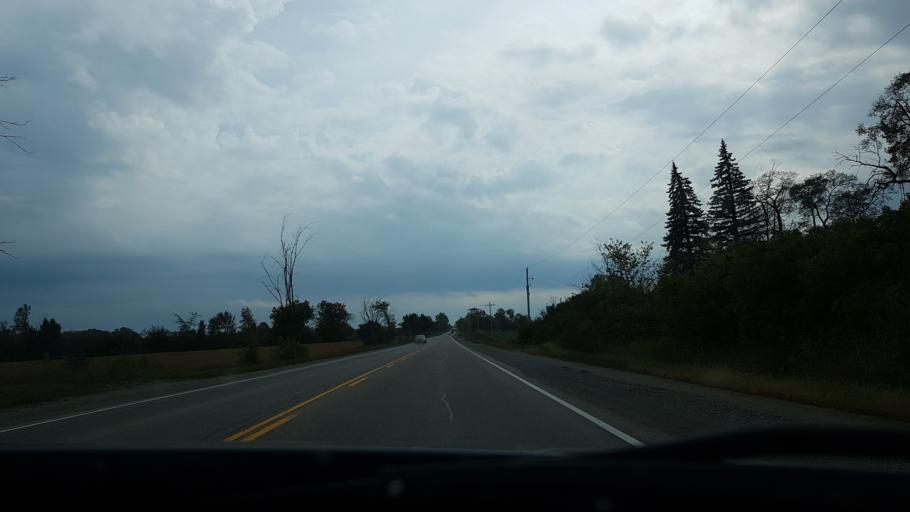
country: CA
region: Ontario
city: Omemee
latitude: 44.4761
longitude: -78.7605
